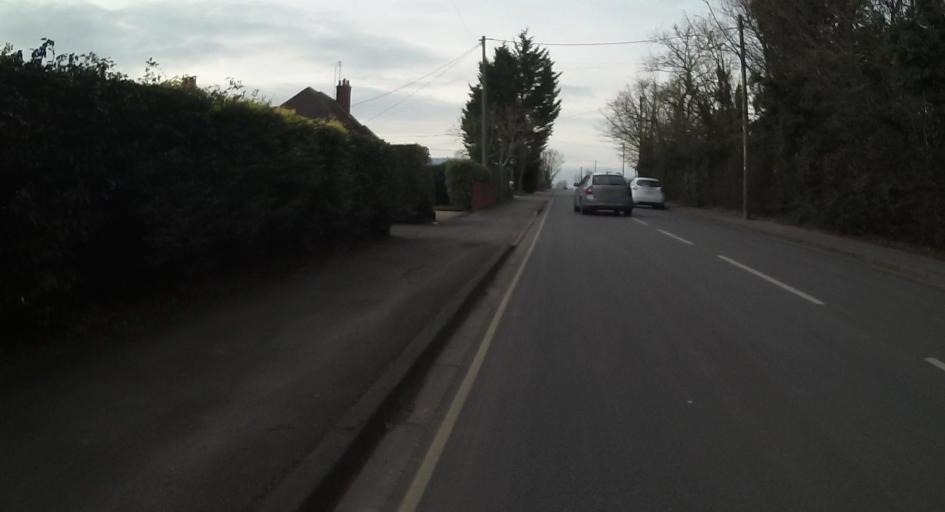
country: GB
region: England
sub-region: West Berkshire
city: Calcot
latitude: 51.4122
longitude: -1.0463
